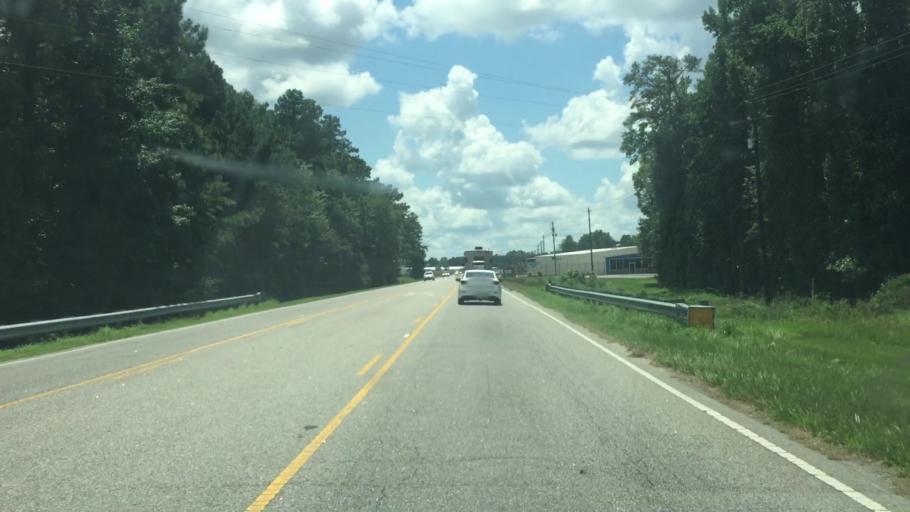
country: US
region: North Carolina
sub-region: Columbus County
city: Tabor City
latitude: 34.1492
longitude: -78.8619
